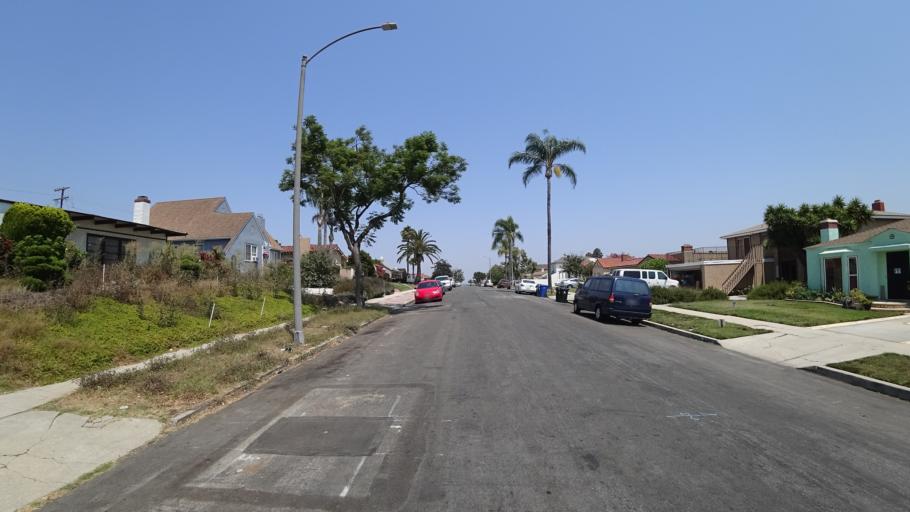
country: US
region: California
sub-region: Los Angeles County
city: View Park-Windsor Hills
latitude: 33.9835
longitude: -118.3500
